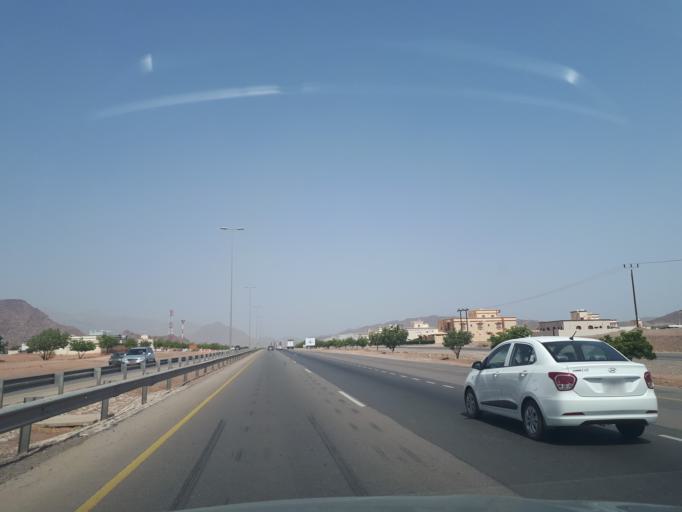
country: OM
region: Muhafazat ad Dakhiliyah
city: Bidbid
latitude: 23.4628
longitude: 58.1591
